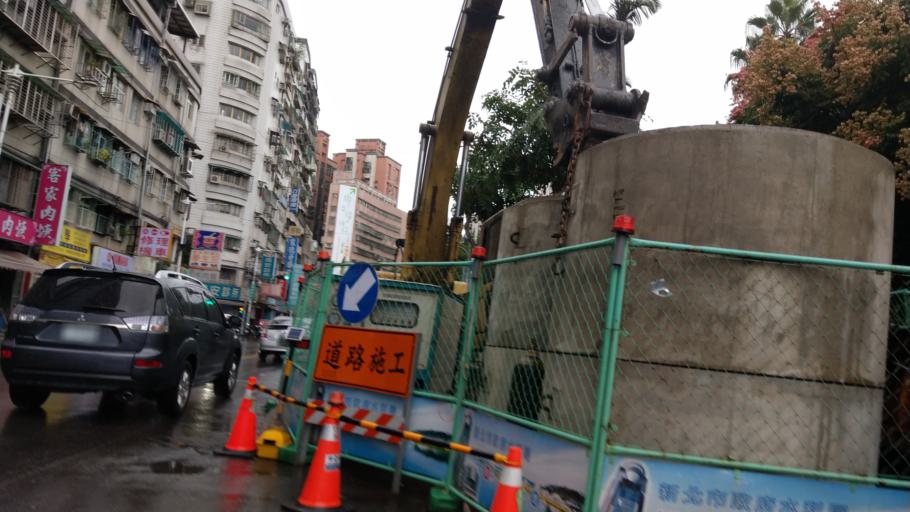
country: TW
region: Taipei
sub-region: Taipei
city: Banqiao
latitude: 24.9986
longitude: 121.4633
